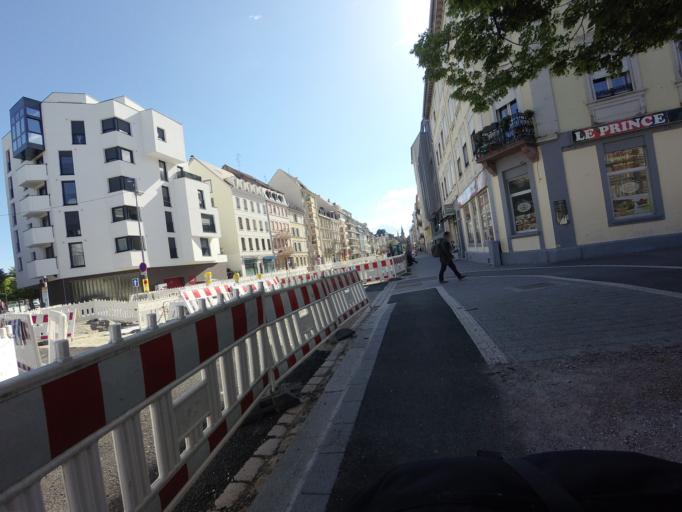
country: FR
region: Alsace
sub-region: Departement du Bas-Rhin
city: Strasbourg
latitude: 48.5821
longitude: 7.7328
